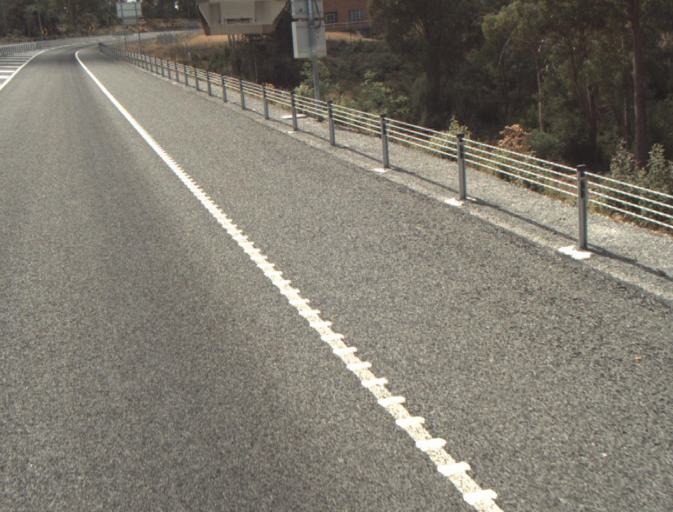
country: AU
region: Tasmania
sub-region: Launceston
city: Mayfield
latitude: -41.3007
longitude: 147.0499
